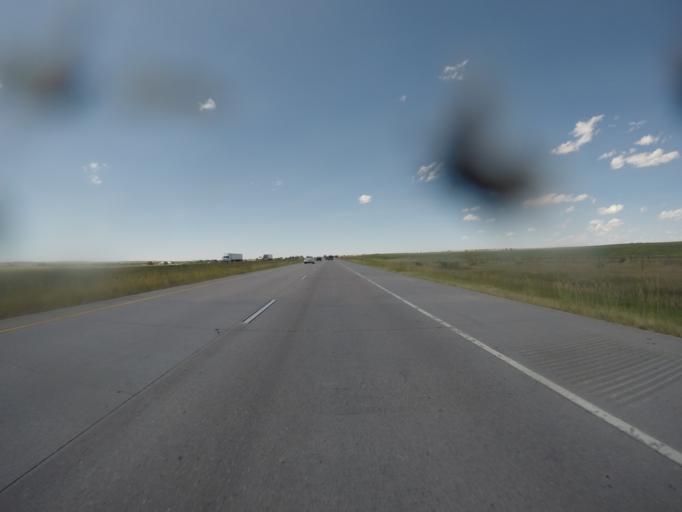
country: US
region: Colorado
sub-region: Arapahoe County
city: Byers
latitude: 39.6009
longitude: -104.0346
